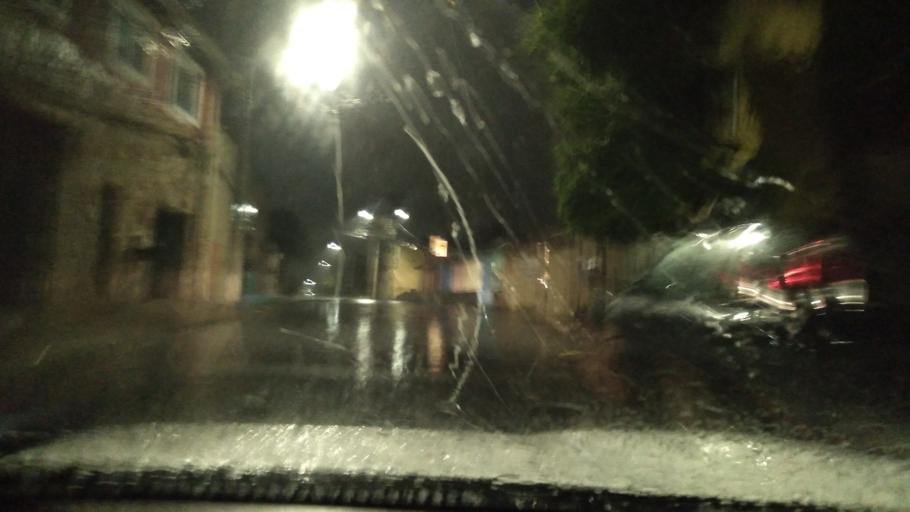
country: BR
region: Minas Gerais
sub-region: Belo Horizonte
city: Belo Horizonte
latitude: -19.8762
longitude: -43.9482
